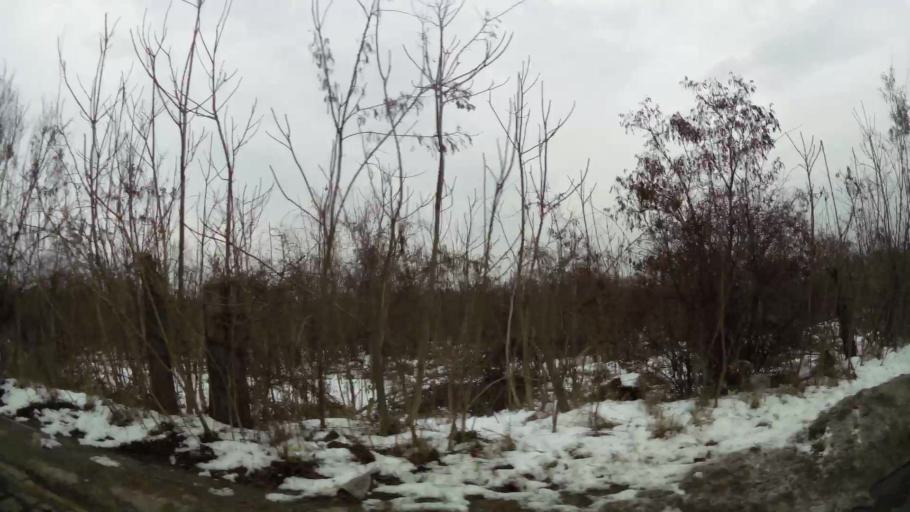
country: MK
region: Butel
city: Butel
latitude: 42.0371
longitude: 21.4368
